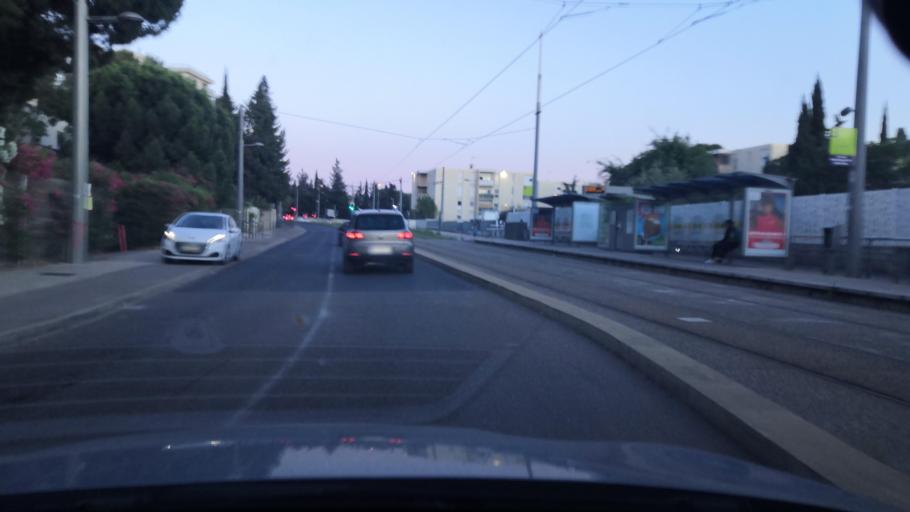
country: FR
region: Languedoc-Roussillon
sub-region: Departement de l'Herault
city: Juvignac
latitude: 43.6177
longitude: 3.8397
